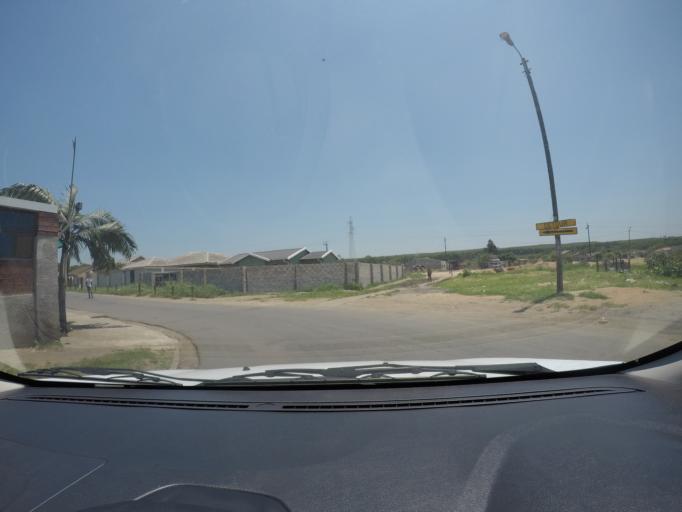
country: ZA
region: KwaZulu-Natal
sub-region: uThungulu District Municipality
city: eSikhawini
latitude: -28.8742
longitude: 31.8977
